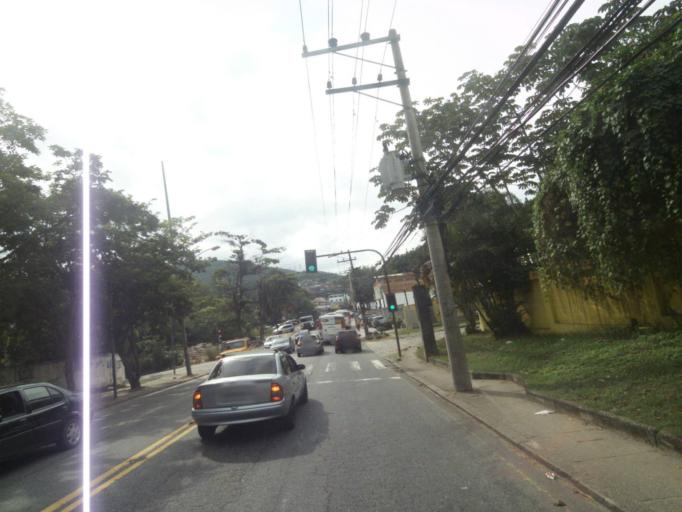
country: BR
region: Rio de Janeiro
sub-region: Sao Joao De Meriti
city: Sao Joao de Meriti
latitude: -22.9115
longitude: -43.3778
